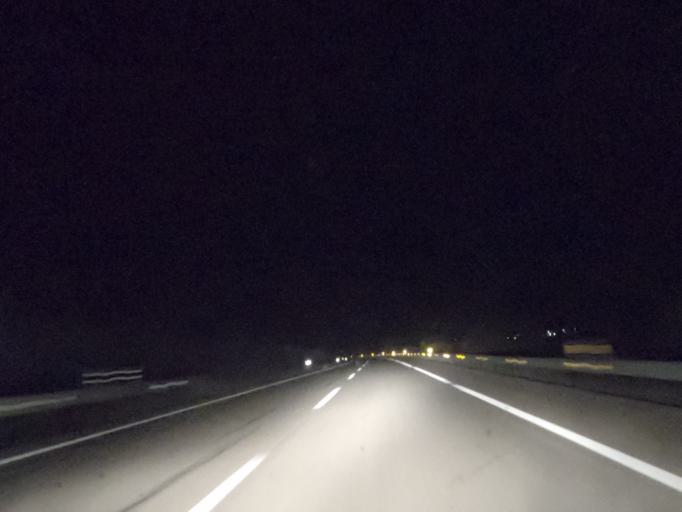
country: ES
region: Castille and Leon
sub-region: Provincia de Zamora
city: Quiruelas de Vidriales
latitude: 42.0272
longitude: -5.8258
